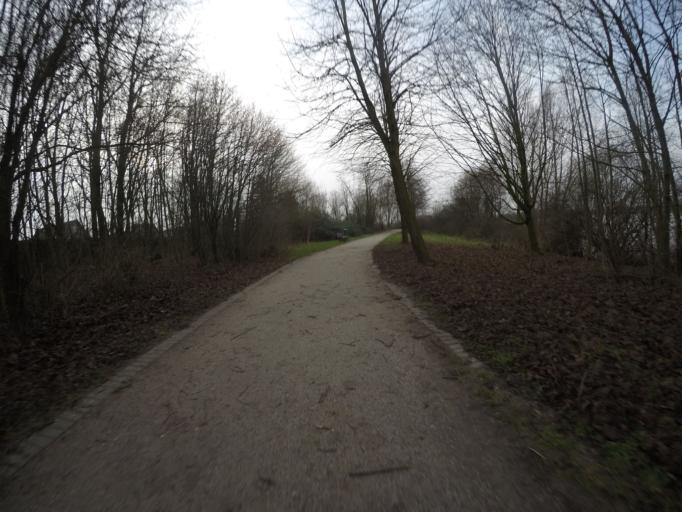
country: DE
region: North Rhine-Westphalia
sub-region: Regierungsbezirk Dusseldorf
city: Xanten
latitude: 51.6758
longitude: 6.4536
